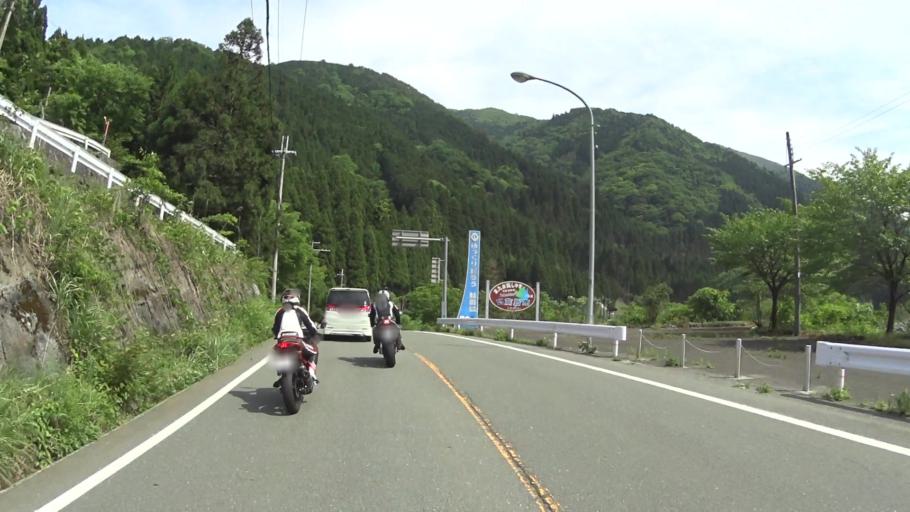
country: JP
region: Shiga Prefecture
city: Kitahama
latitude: 35.2895
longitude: 135.8836
